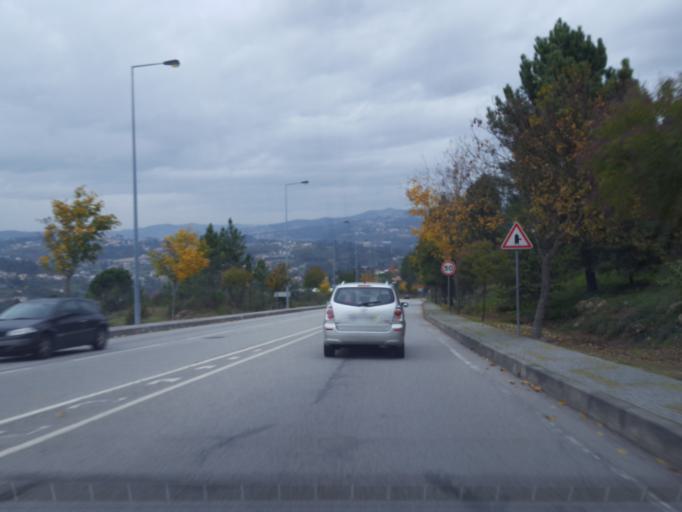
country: PT
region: Porto
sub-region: Marco de Canaveses
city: Marco de Canavezes
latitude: 41.1824
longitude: -8.1569
